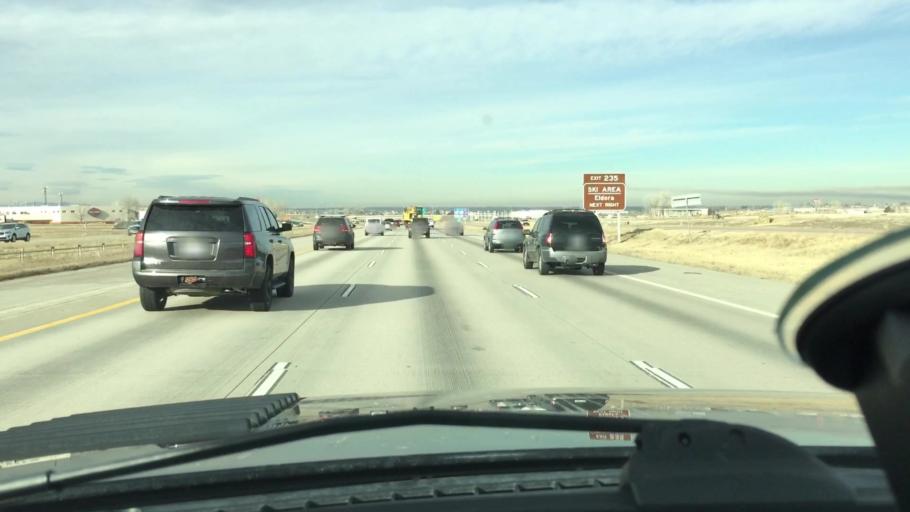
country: US
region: Colorado
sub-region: Weld County
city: Dacono
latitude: 40.0780
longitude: -104.9787
